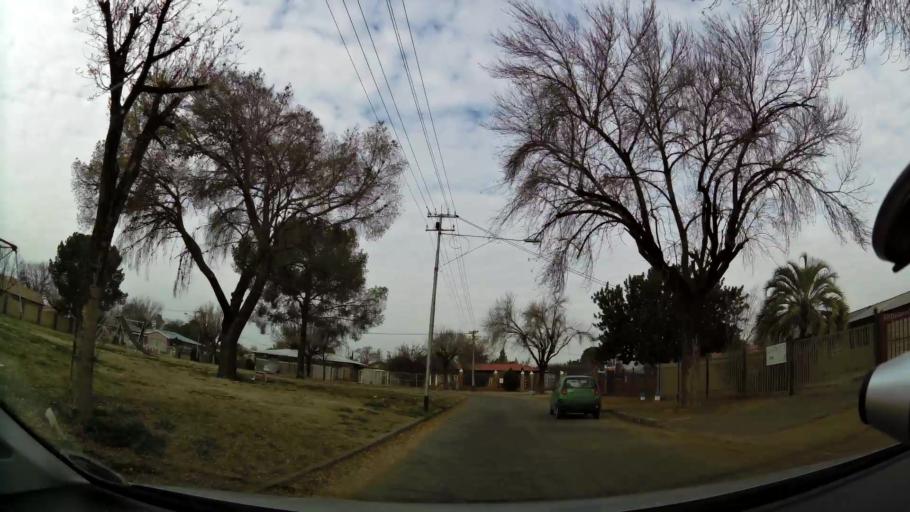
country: ZA
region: Orange Free State
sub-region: Mangaung Metropolitan Municipality
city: Bloemfontein
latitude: -29.1297
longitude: 26.1870
